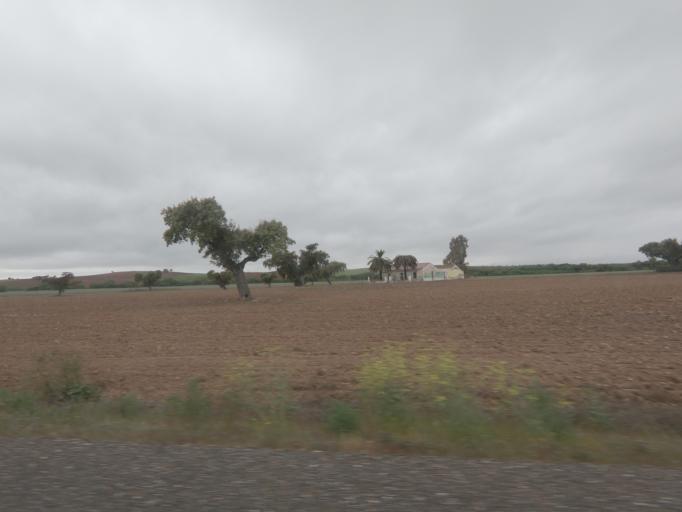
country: ES
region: Extremadura
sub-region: Provincia de Badajoz
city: La Roca de la Sierra
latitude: 39.0602
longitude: -6.7687
